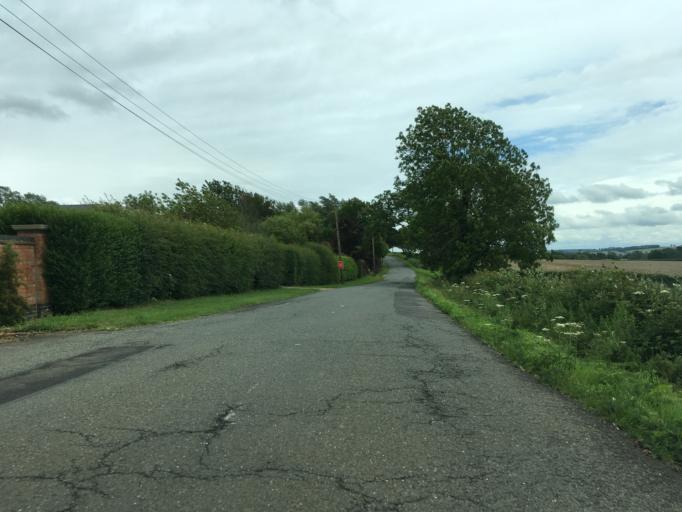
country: GB
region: England
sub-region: Northamptonshire
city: Daventry
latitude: 52.2425
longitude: -1.1934
